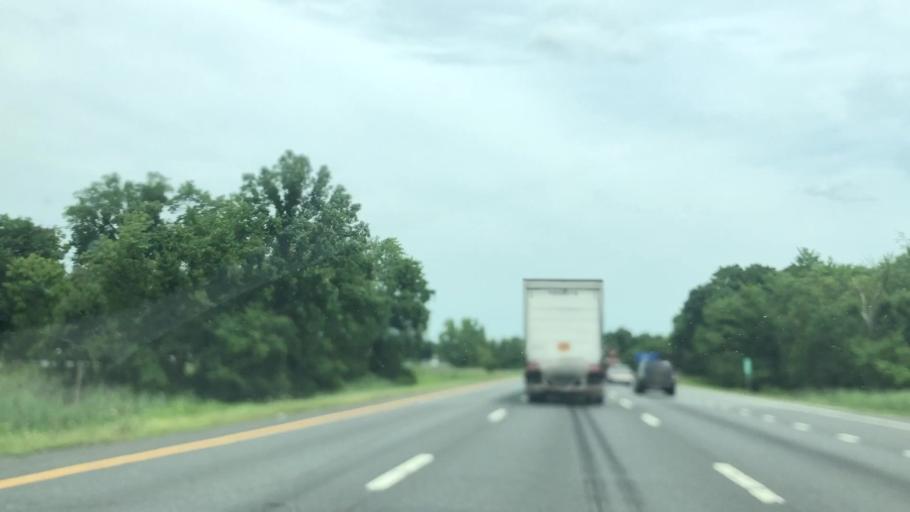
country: US
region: New York
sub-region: Albany County
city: Roessleville
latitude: 42.7333
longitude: -73.7878
